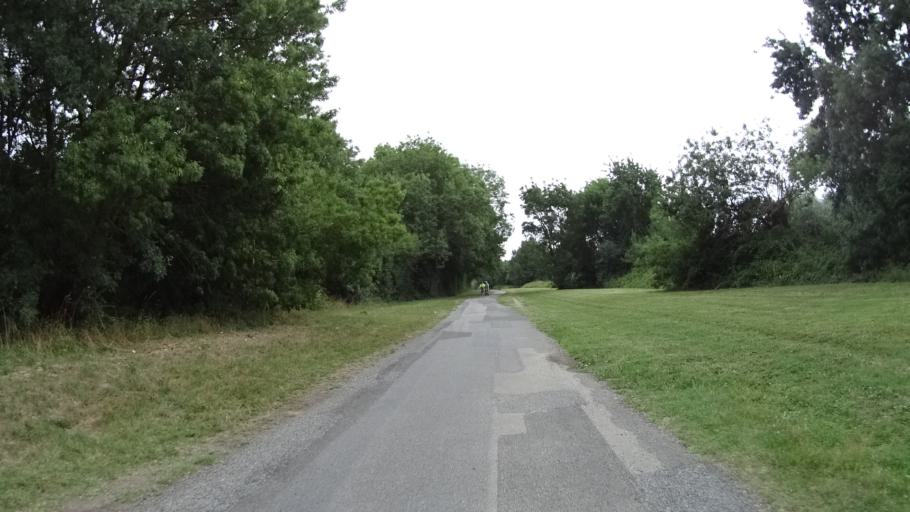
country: FR
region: Pays de la Loire
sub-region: Departement de la Loire-Atlantique
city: Thouare-sur-Loire
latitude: 47.2548
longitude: -1.4456
